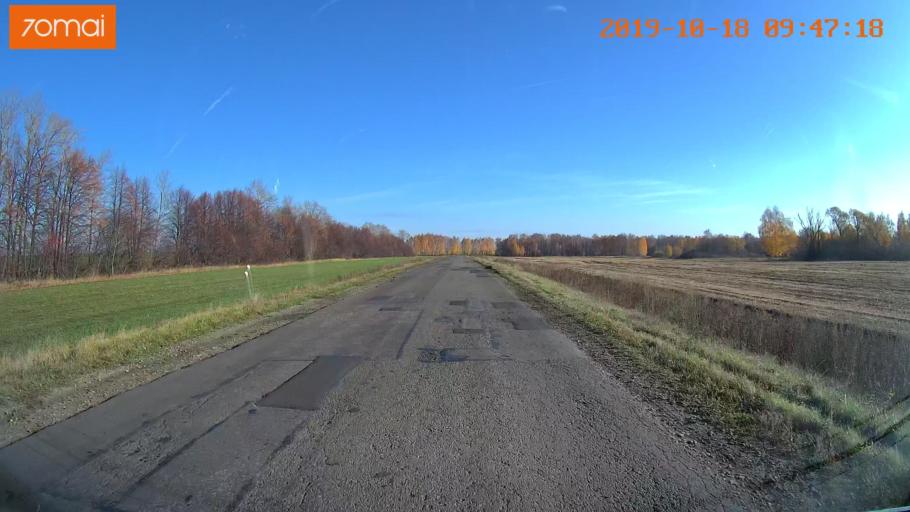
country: RU
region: Tula
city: Kazachka
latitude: 53.3175
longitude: 38.2289
